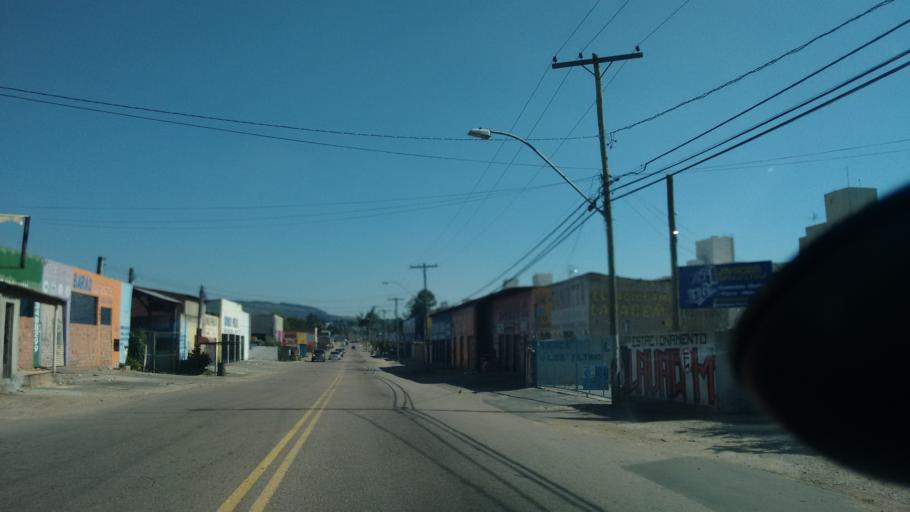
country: BR
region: Rio Grande do Sul
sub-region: Cachoeirinha
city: Cachoeirinha
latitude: -30.0072
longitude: -51.1279
